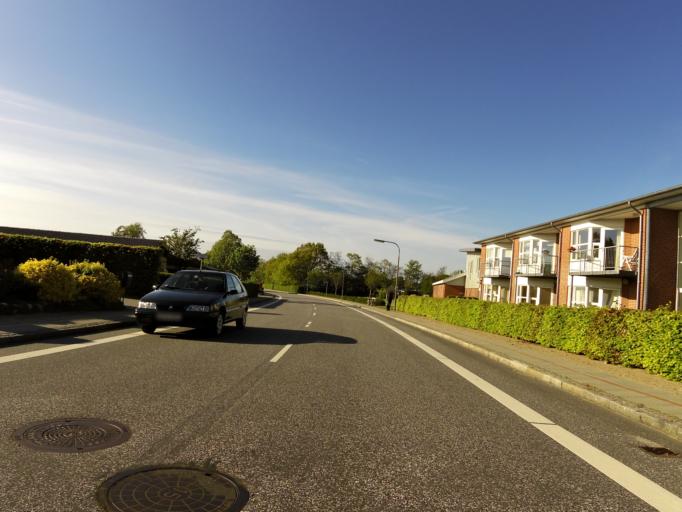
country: DK
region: South Denmark
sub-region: Tonder Kommune
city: Toftlund
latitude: 55.1851
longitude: 9.0635
